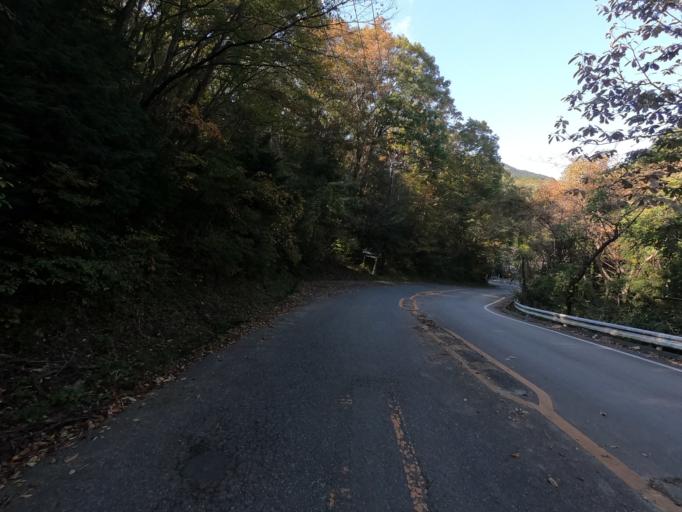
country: JP
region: Ibaraki
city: Tsukuba
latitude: 36.2265
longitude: 140.1258
